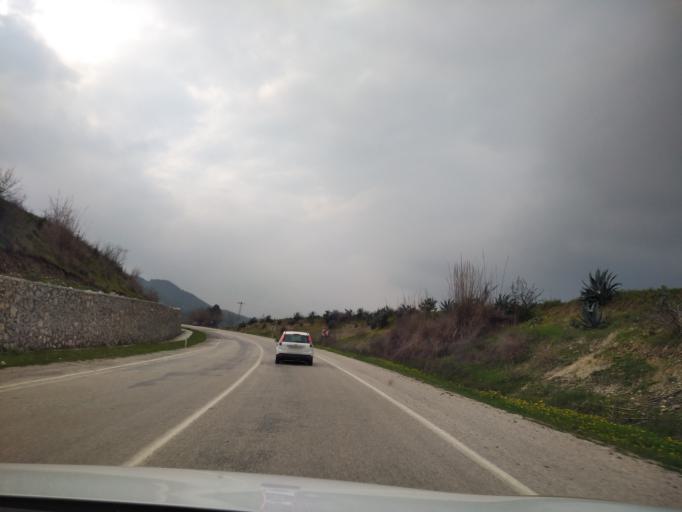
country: TR
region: Mersin
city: Yenice
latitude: 37.0946
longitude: 35.1333
